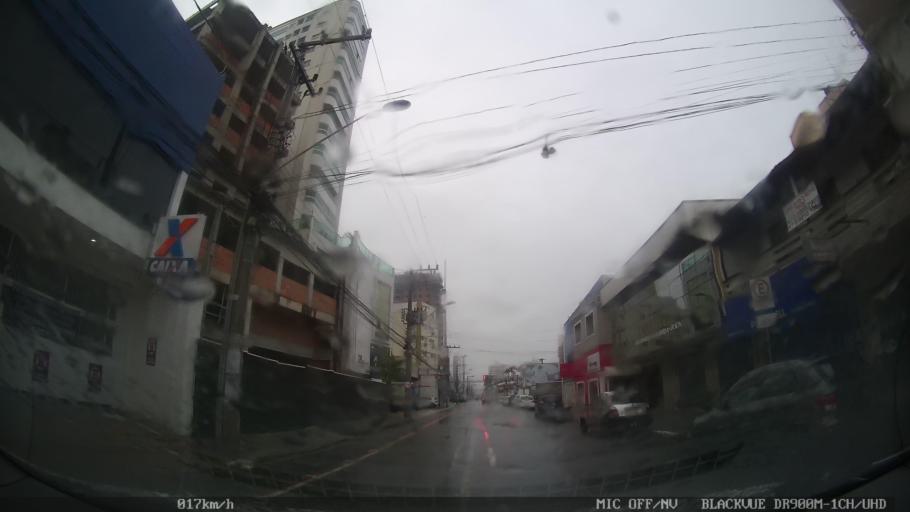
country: BR
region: Santa Catarina
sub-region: Itajai
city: Itajai
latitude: -26.9089
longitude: -48.6636
